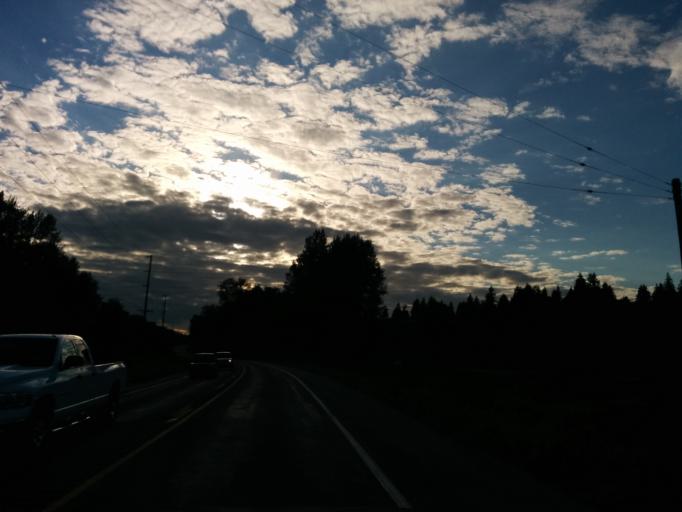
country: US
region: Washington
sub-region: Snohomish County
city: Monroe
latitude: 47.8568
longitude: -121.9455
